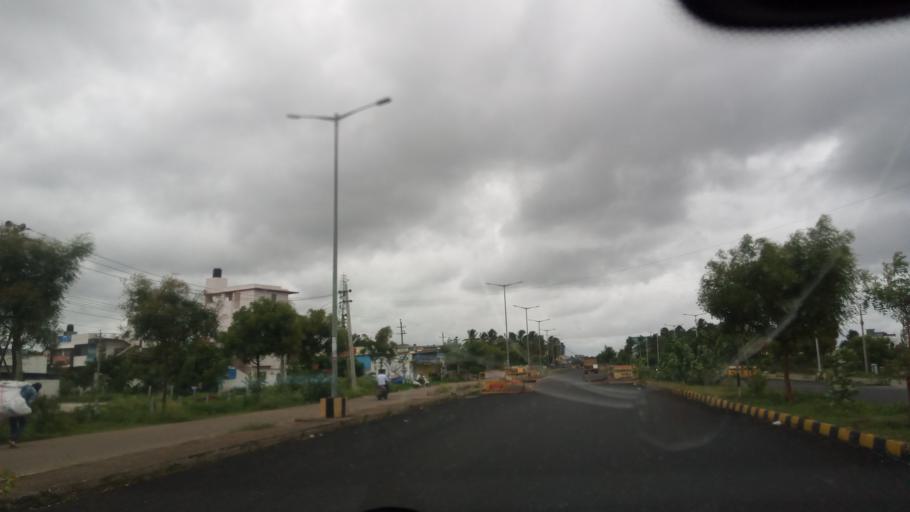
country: IN
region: Karnataka
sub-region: Mysore
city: Mysore
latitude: 12.2911
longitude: 76.6055
